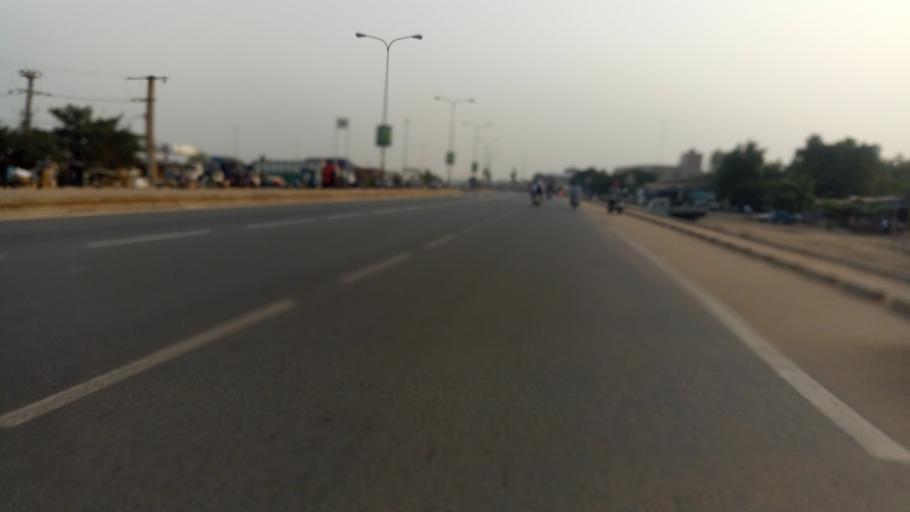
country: TG
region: Maritime
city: Lome
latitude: 6.2623
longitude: 1.2081
